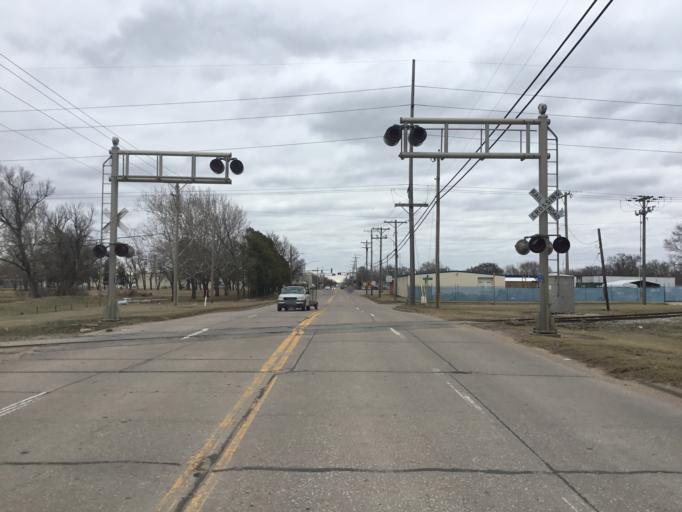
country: US
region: Kansas
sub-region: Sedgwick County
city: Wichita
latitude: 37.6659
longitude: -97.3809
